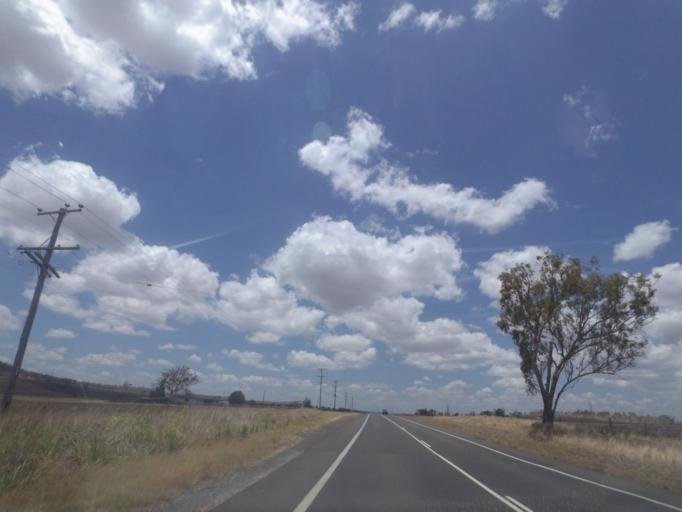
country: AU
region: Queensland
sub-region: Toowoomba
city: Top Camp
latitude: -27.7374
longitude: 151.9185
